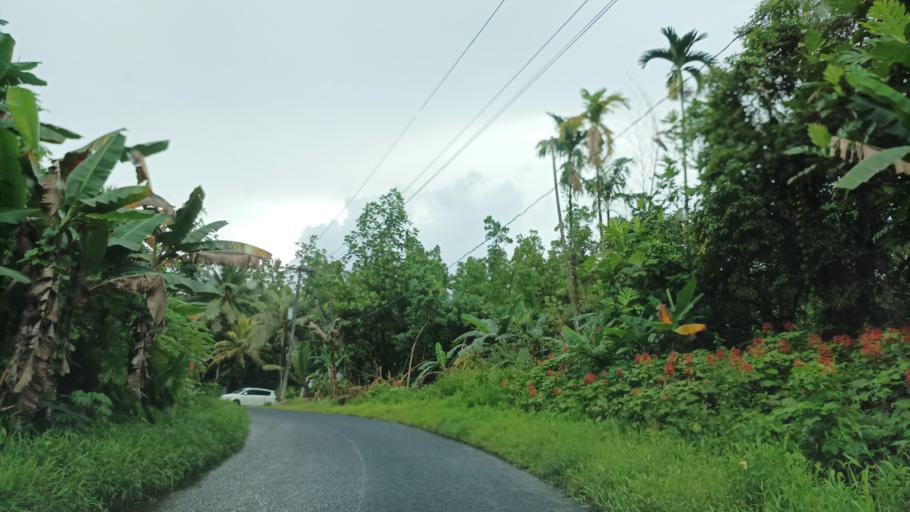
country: FM
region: Pohnpei
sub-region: Sokehs Municipality
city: Palikir - National Government Center
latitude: 6.8330
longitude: 158.1541
